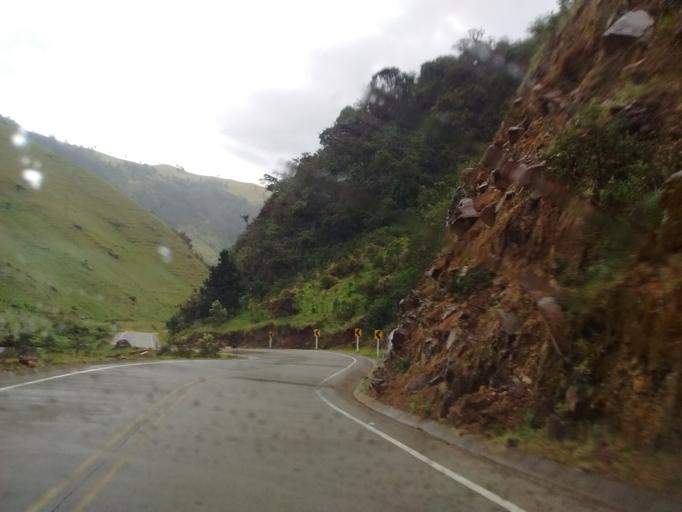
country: CO
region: Cauca
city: Paispamba
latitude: 2.2979
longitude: -76.5108
